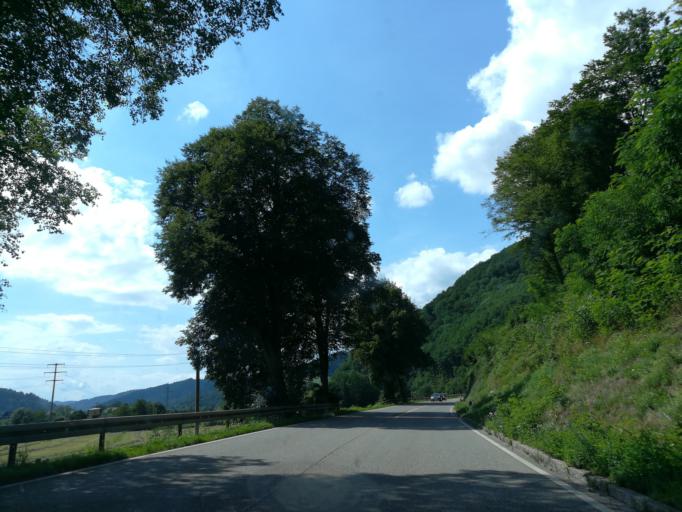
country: DE
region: Baden-Wuerttemberg
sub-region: Freiburg Region
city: Wolfach
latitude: 48.2830
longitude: 8.2048
